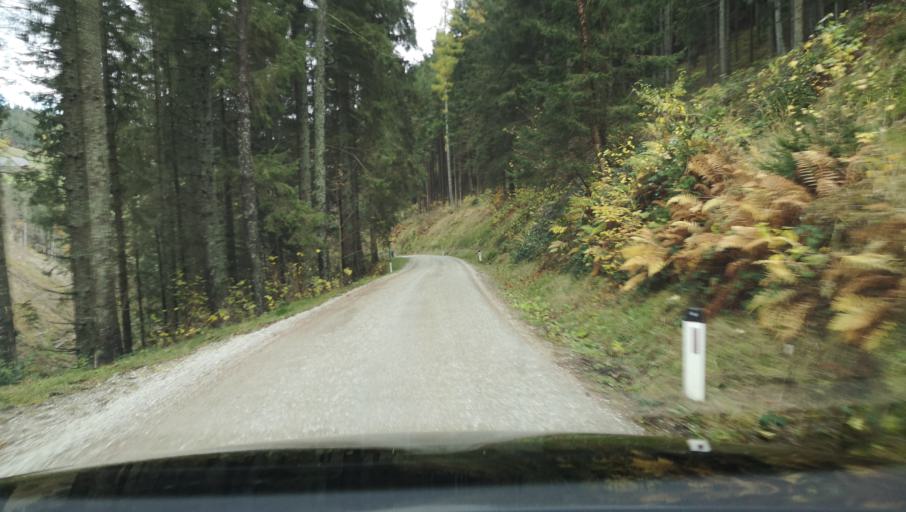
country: AT
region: Styria
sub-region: Politischer Bezirk Weiz
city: Gasen
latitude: 47.3763
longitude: 15.6167
